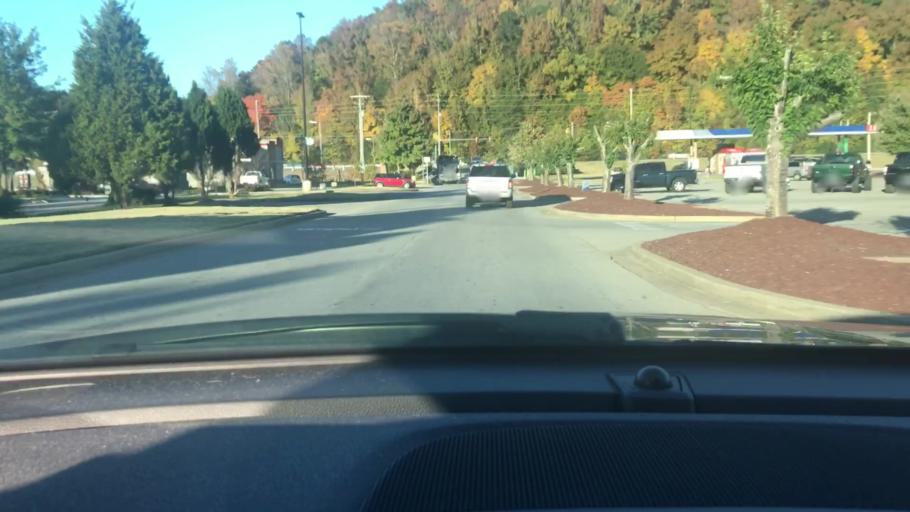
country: US
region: Tennessee
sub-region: Cheatham County
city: Ashland City
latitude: 36.2489
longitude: -87.0340
